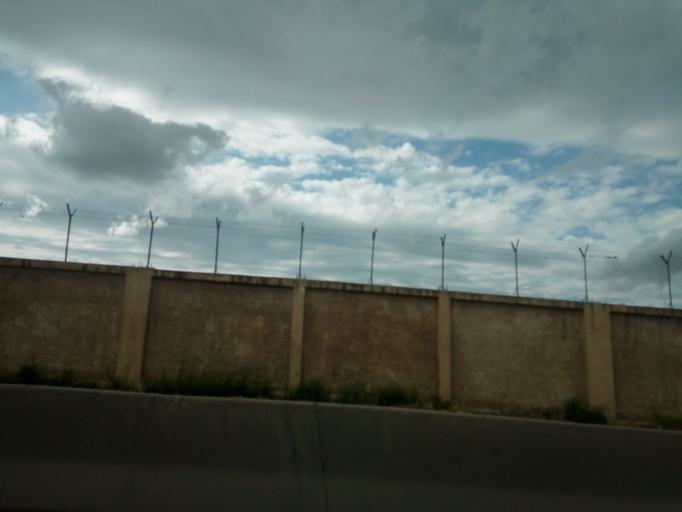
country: DZ
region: Tipaza
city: Douera
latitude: 36.6266
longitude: 2.9450
